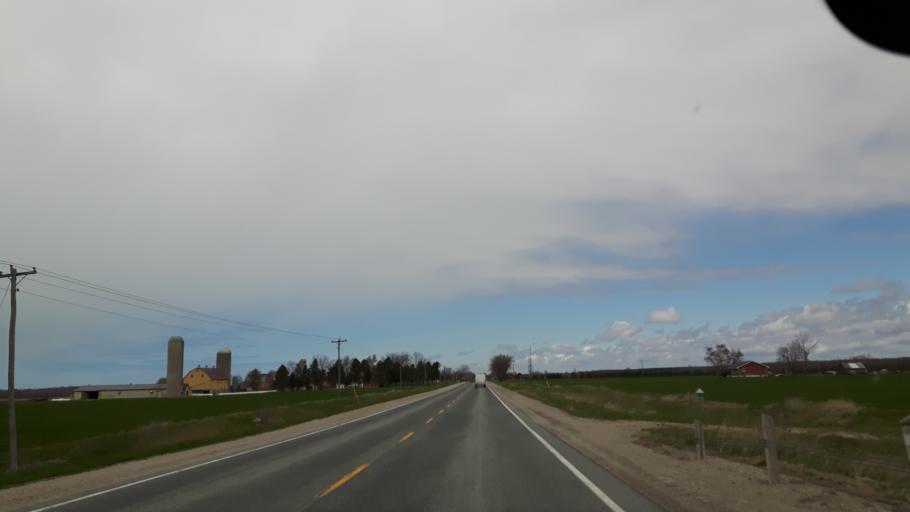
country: CA
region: Ontario
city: Bluewater
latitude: 43.4802
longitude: -81.6979
